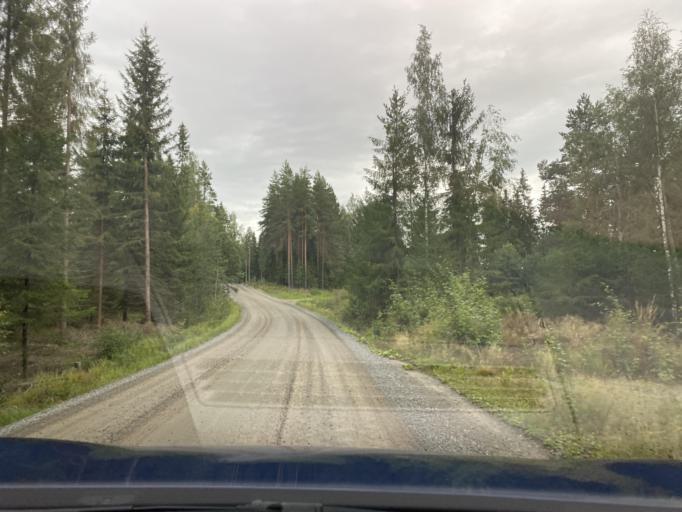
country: FI
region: Pirkanmaa
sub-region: Lounais-Pirkanmaa
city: Punkalaidun
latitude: 61.2495
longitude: 23.0375
